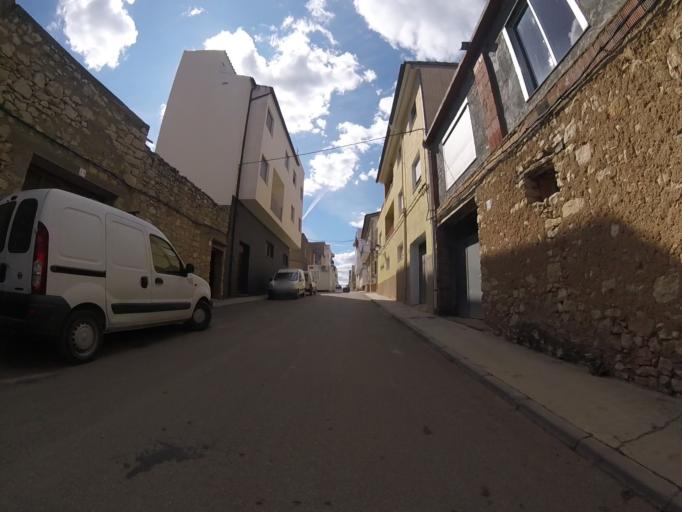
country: ES
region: Valencia
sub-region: Provincia de Castello
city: Cati
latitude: 40.4238
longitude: 0.0795
